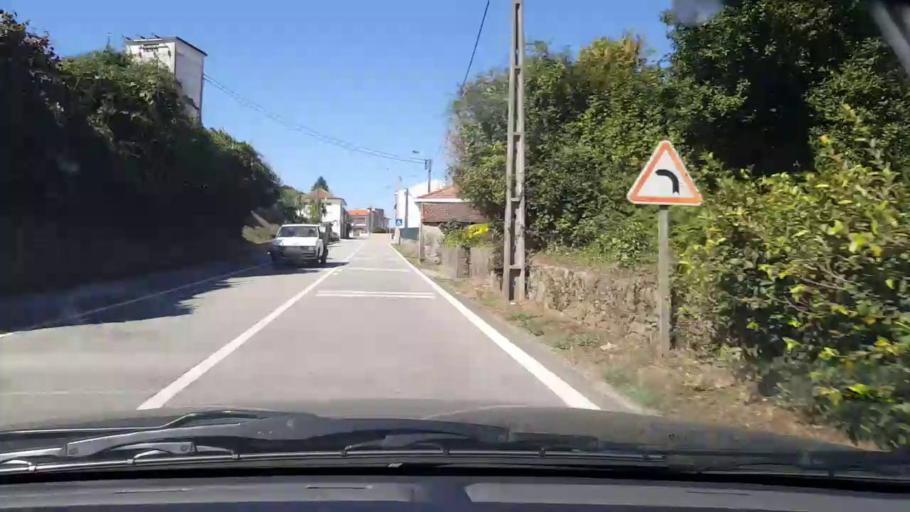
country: PT
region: Porto
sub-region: Maia
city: Gemunde
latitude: 41.3392
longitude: -8.6379
